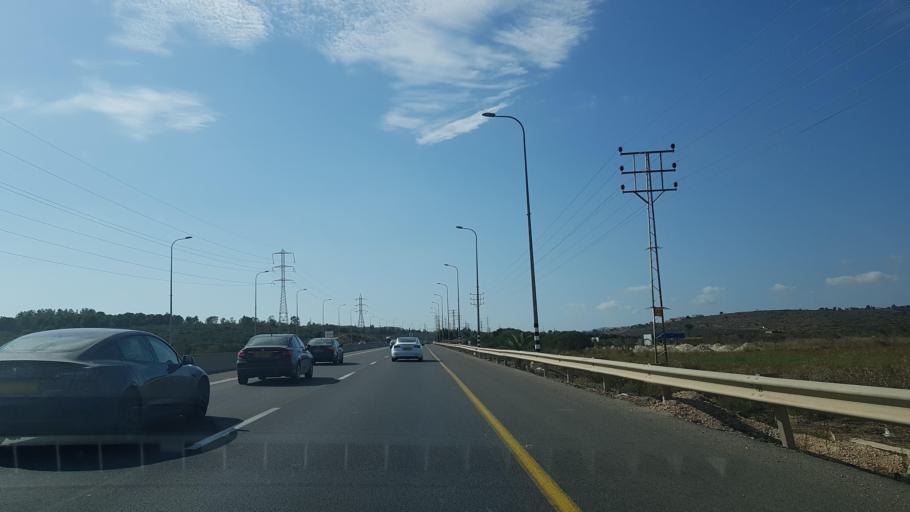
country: IL
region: Northern District
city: Kafr Kanna
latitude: 32.7634
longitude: 35.3305
